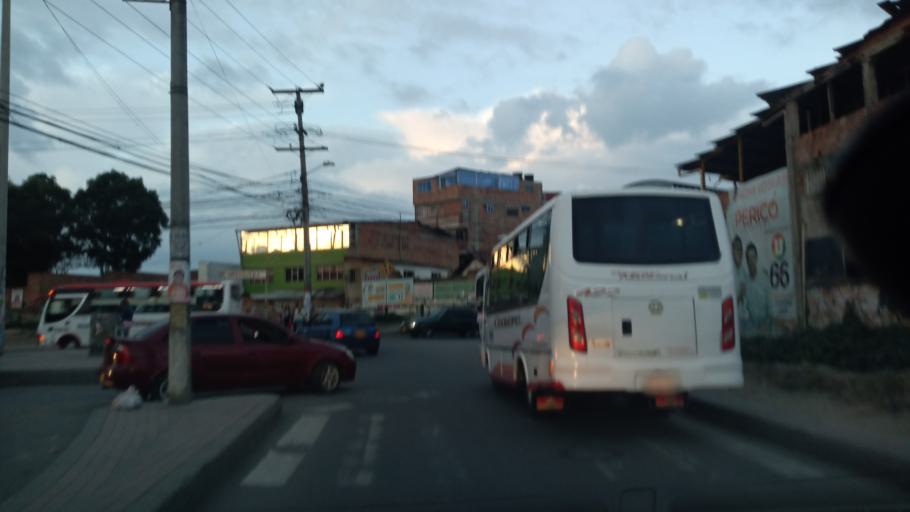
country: CO
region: Cundinamarca
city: Soacha
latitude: 4.5807
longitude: -74.2215
